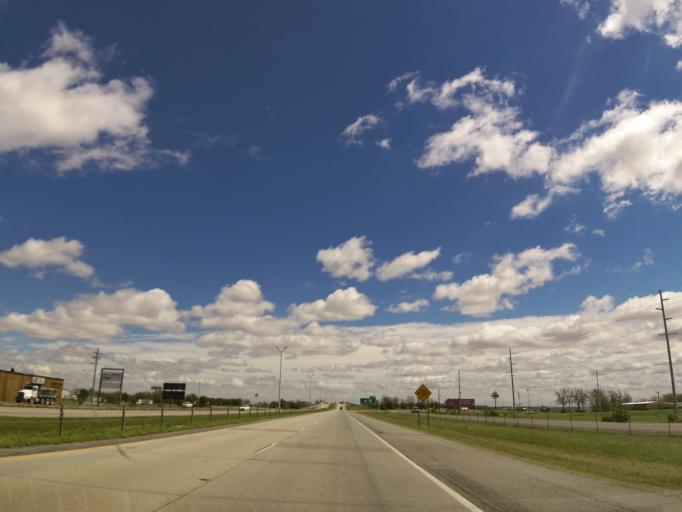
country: US
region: Arkansas
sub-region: Craighead County
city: Jonesboro
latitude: 35.8069
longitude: -90.6451
